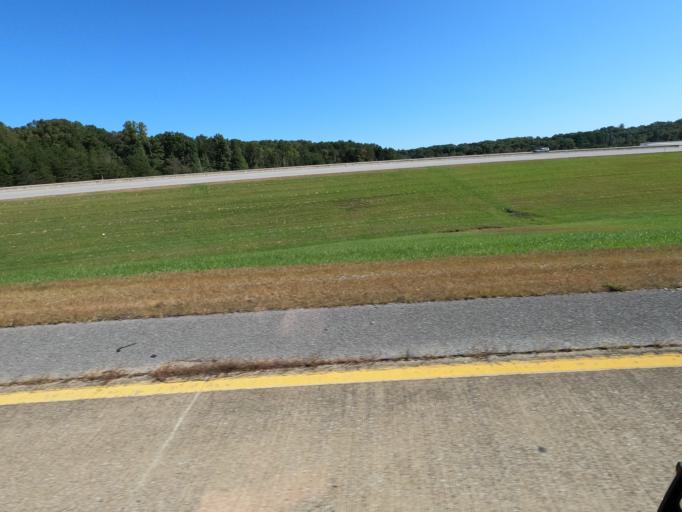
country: US
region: Tennessee
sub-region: Hamilton County
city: Soddy-Daisy
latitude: 35.3024
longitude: -85.1528
